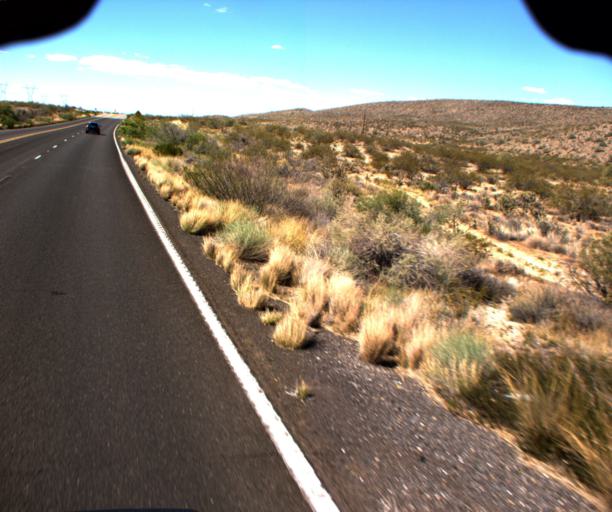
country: US
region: Arizona
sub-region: Mohave County
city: Kingman
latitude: 34.9445
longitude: -113.6664
